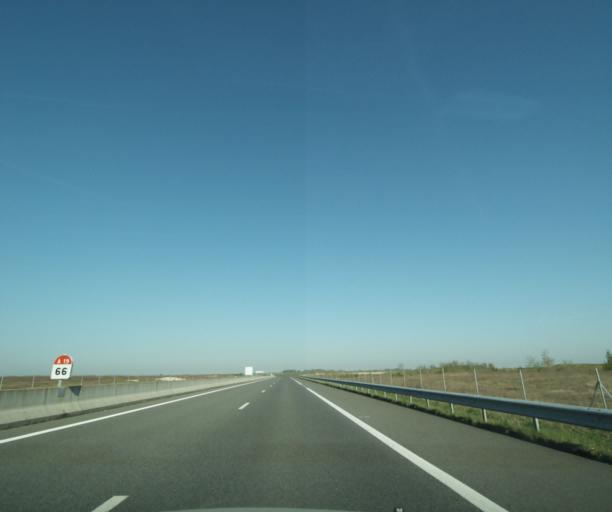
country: FR
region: Centre
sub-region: Departement du Loiret
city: Pannes
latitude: 48.0737
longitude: 2.6385
